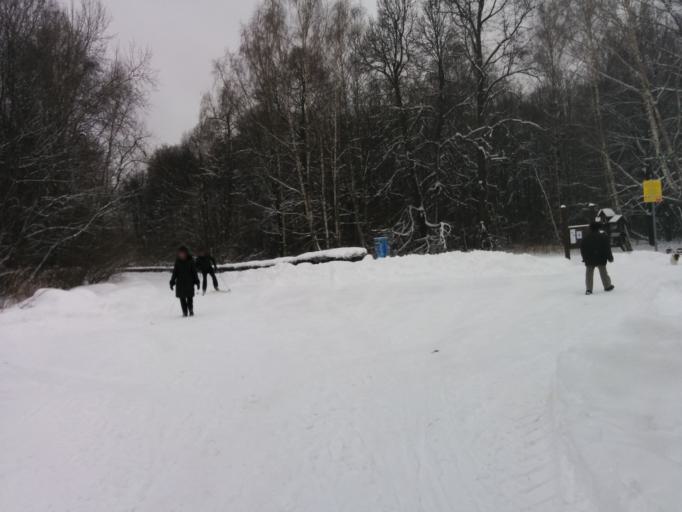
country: RU
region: Moskovskaya
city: Izmaylovo
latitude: 55.7822
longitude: 37.7781
